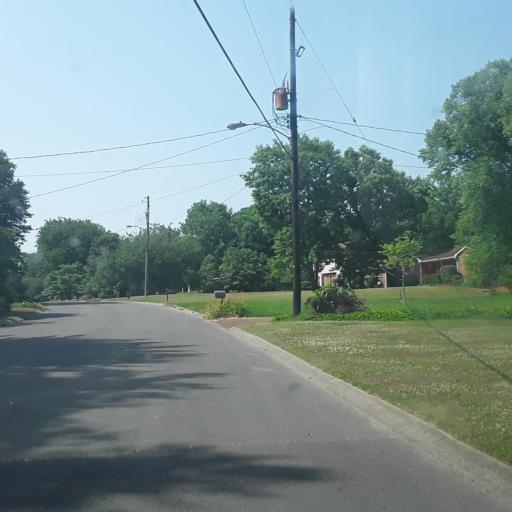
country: US
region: Tennessee
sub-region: Williamson County
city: Brentwood
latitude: 36.0459
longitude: -86.7511
